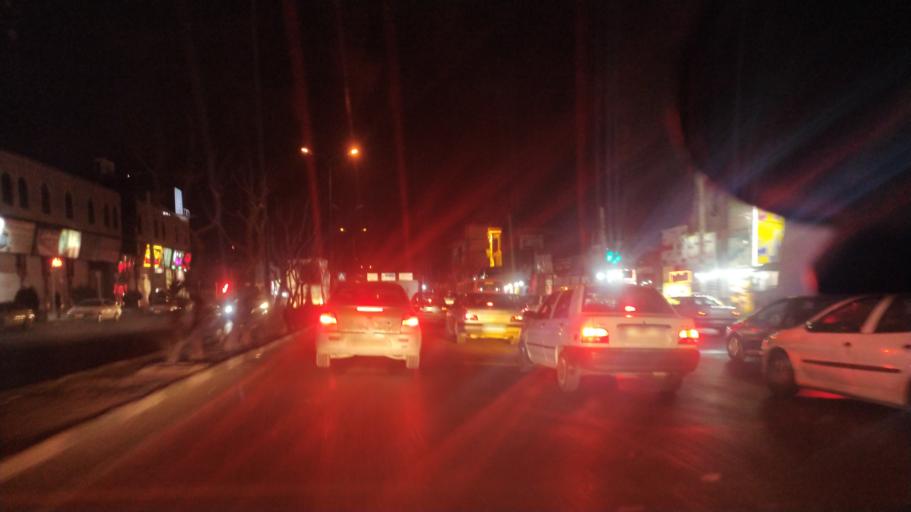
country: IR
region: Alborz
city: Karaj
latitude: 35.7822
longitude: 51.0063
